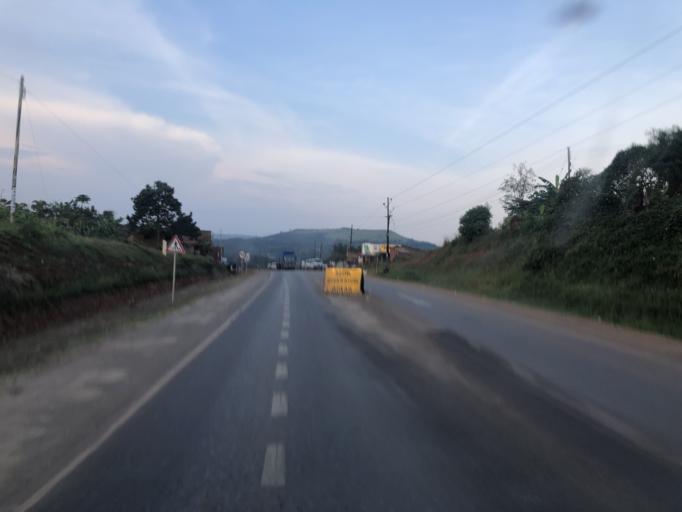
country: UG
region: Central Region
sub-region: Mpigi District
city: Mpigi
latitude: 0.2185
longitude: 32.3323
